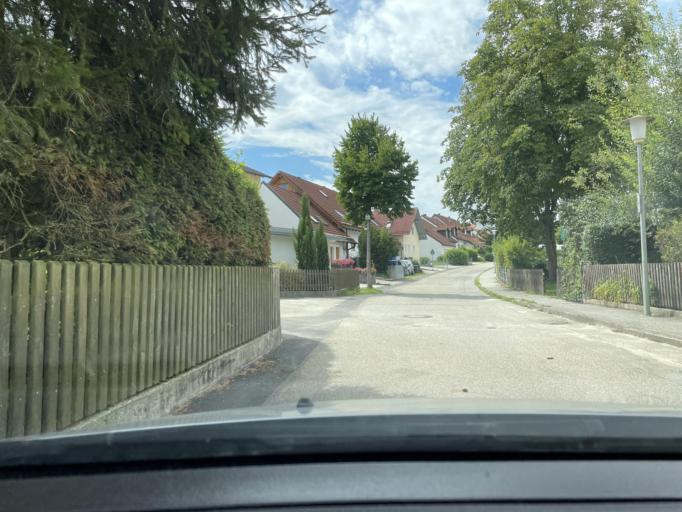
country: DE
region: Bavaria
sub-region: Lower Bavaria
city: Altfraunhofen
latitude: 48.4471
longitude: 12.1769
